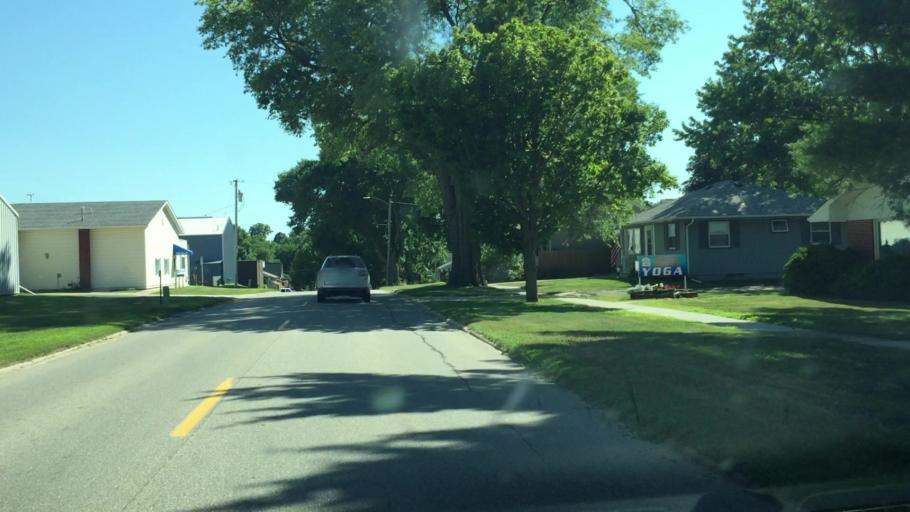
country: US
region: Iowa
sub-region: Linn County
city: Mount Vernon
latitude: 41.9274
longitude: -91.4120
